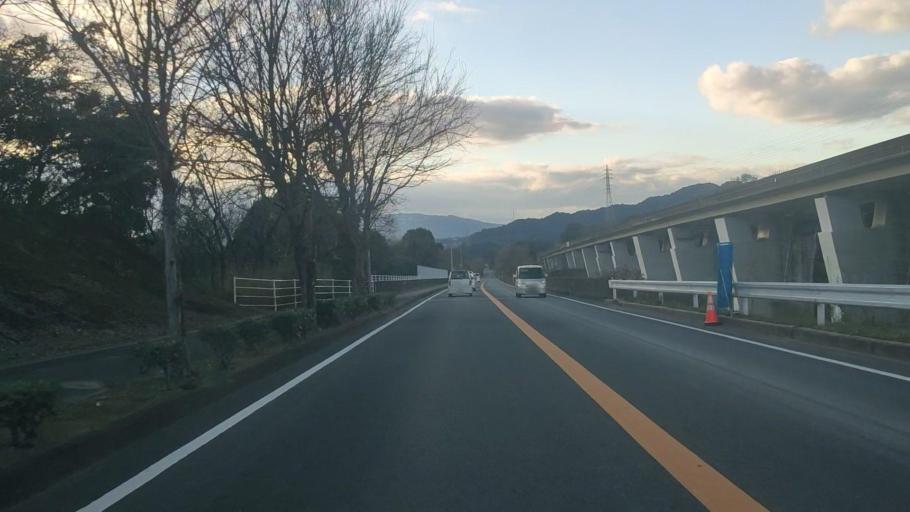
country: JP
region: Saga Prefecture
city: Saga-shi
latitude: 33.2862
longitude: 130.1516
